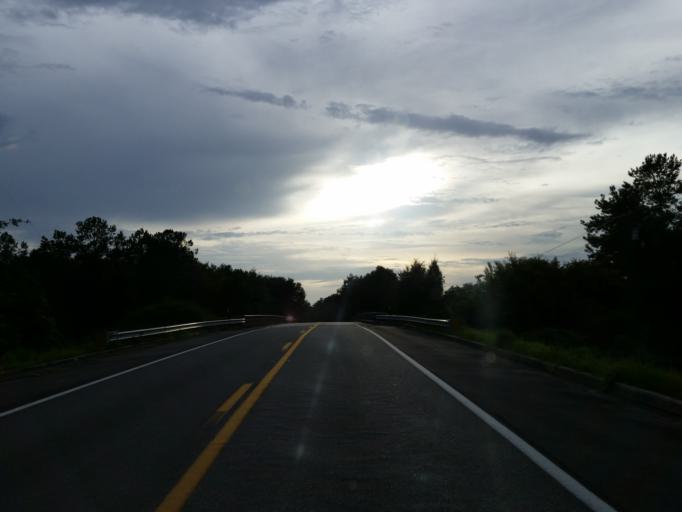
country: US
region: Florida
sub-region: Alachua County
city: High Springs
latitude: 29.9520
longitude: -82.5679
